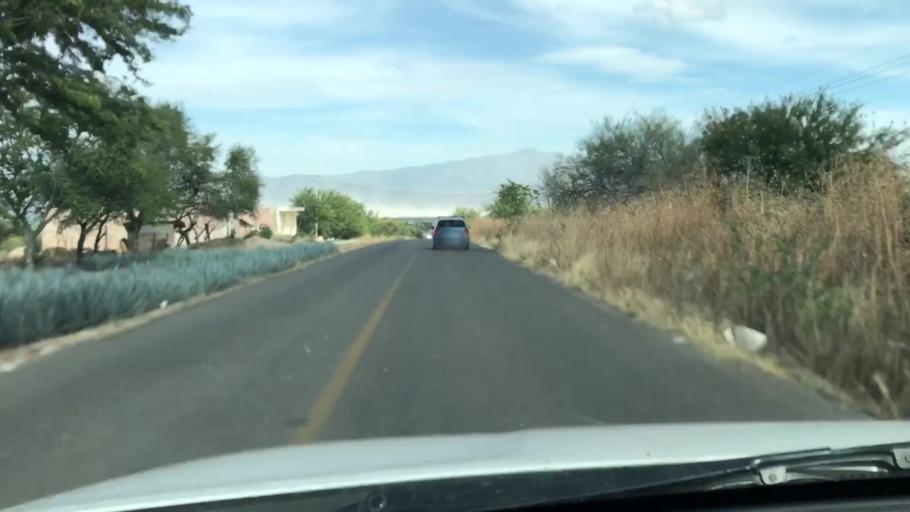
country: MX
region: Jalisco
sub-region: Zacoalco de Torres
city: Barranca de Otates (Barranca de Otatan)
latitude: 20.2745
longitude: -103.6321
